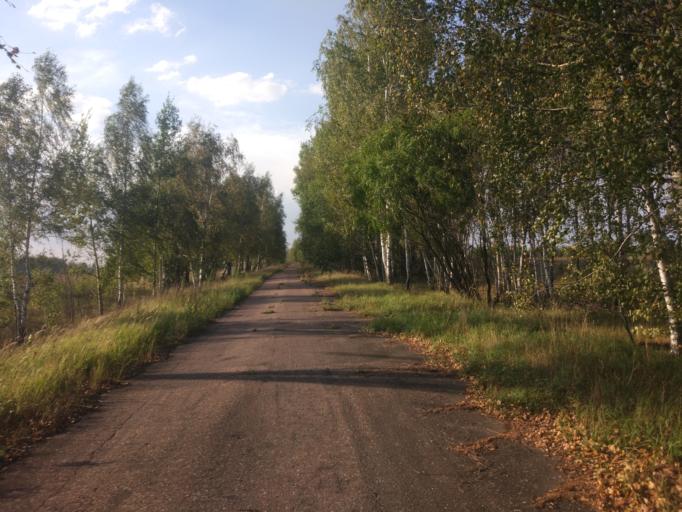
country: RU
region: Brjansk
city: Vyshkov
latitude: 52.6596
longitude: 31.5783
